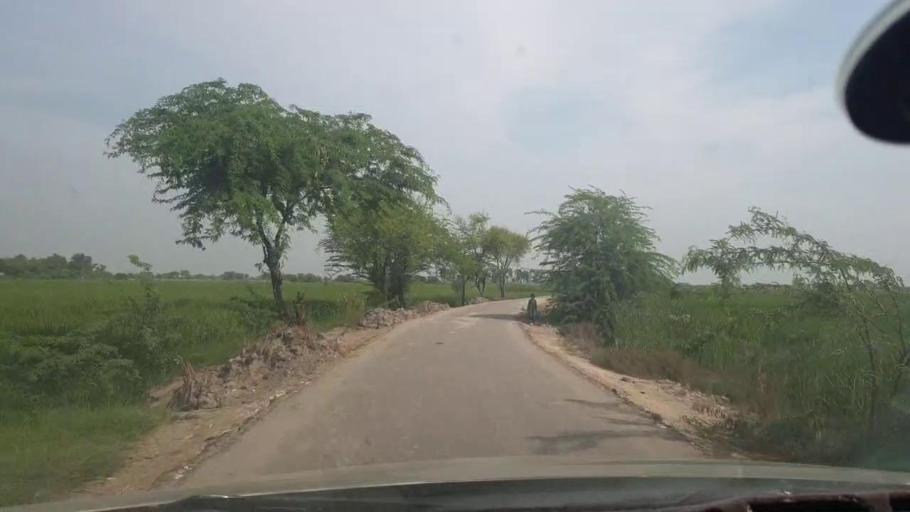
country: PK
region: Sindh
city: Jacobabad
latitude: 28.3054
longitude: 68.4748
